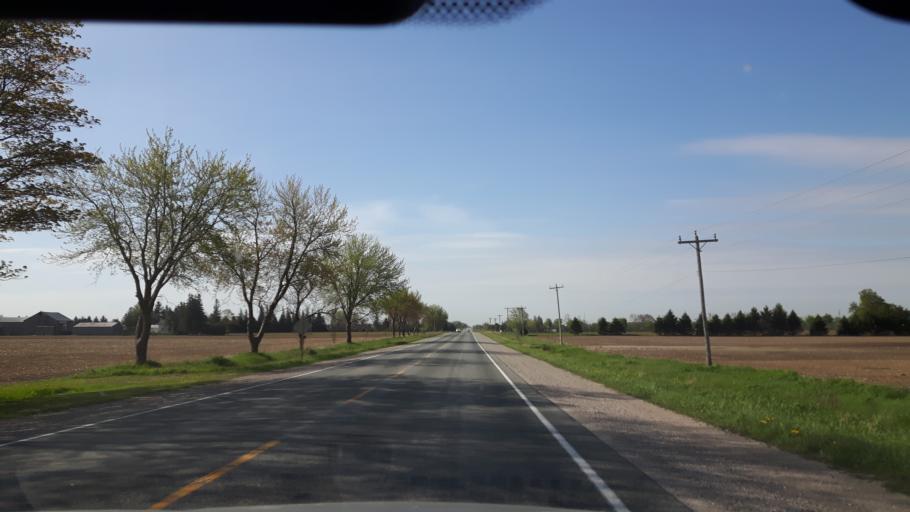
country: CA
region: Ontario
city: Bluewater
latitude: 43.5167
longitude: -81.5155
